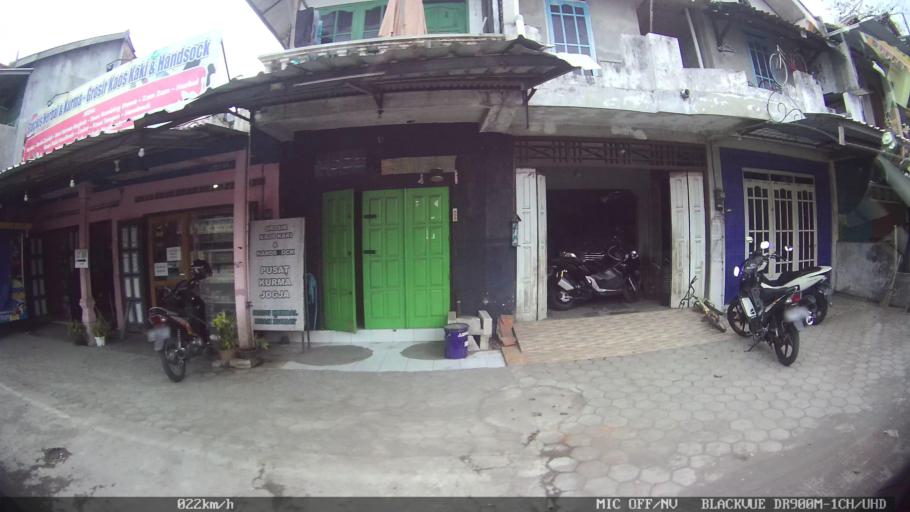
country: ID
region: Daerah Istimewa Yogyakarta
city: Sewon
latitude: -7.8375
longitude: 110.4118
